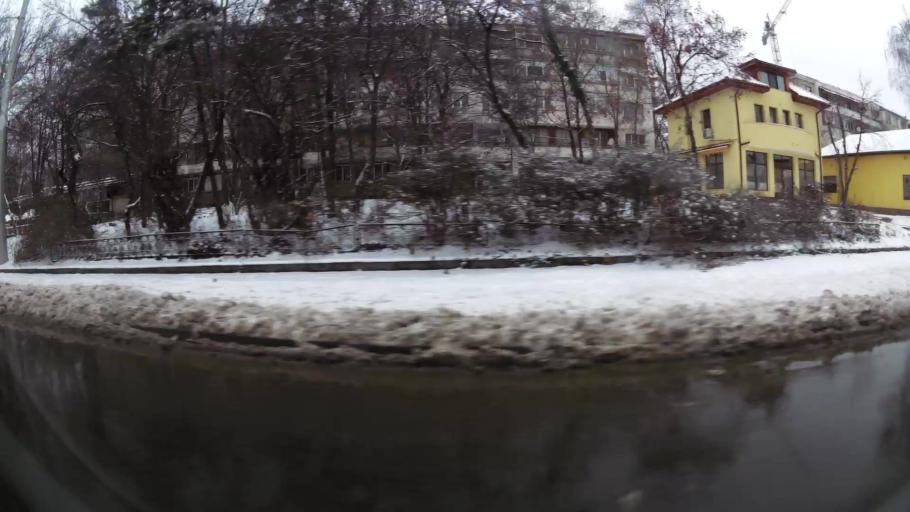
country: BG
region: Sofia-Capital
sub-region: Stolichna Obshtina
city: Sofia
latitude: 42.7058
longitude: 23.2987
